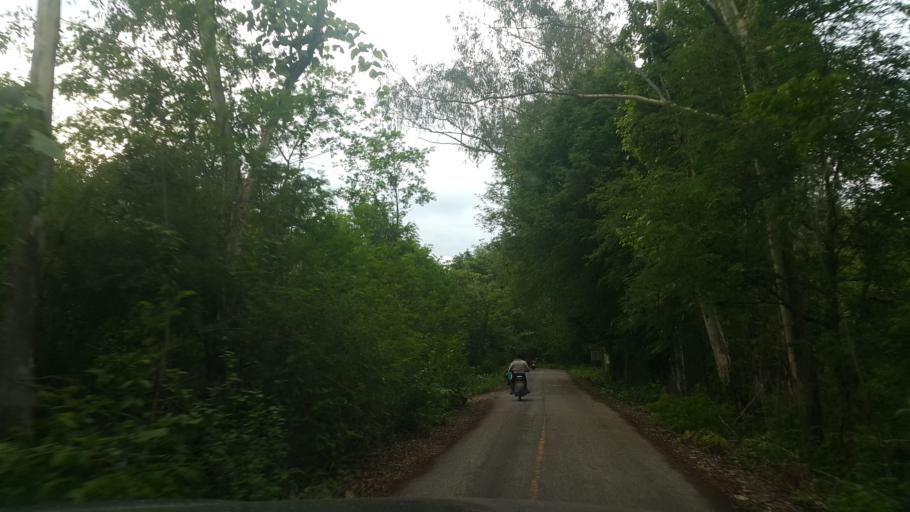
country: TH
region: Chiang Mai
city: Mae On
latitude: 18.7236
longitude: 99.2324
